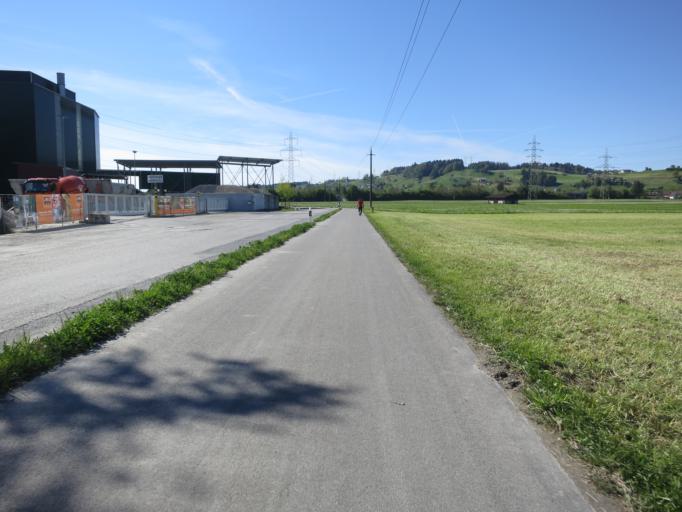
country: CH
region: Saint Gallen
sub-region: Wahlkreis See-Gaster
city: Uznach
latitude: 47.2196
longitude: 8.9688
